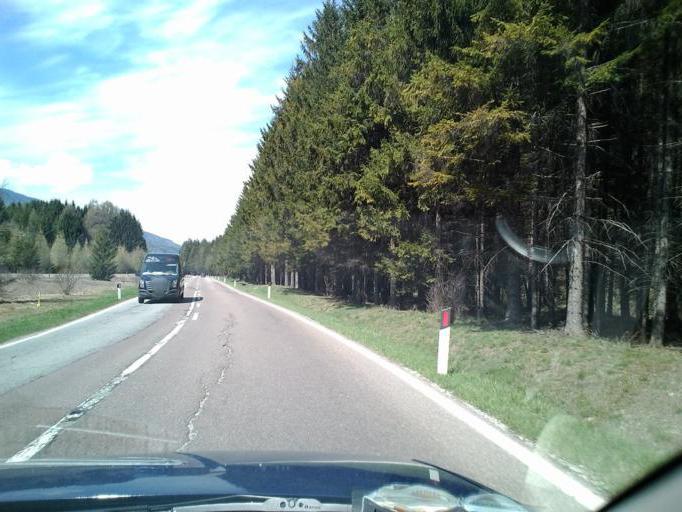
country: IT
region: Trentino-Alto Adige
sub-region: Bolzano
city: Villabassa
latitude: 46.7403
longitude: 12.1493
